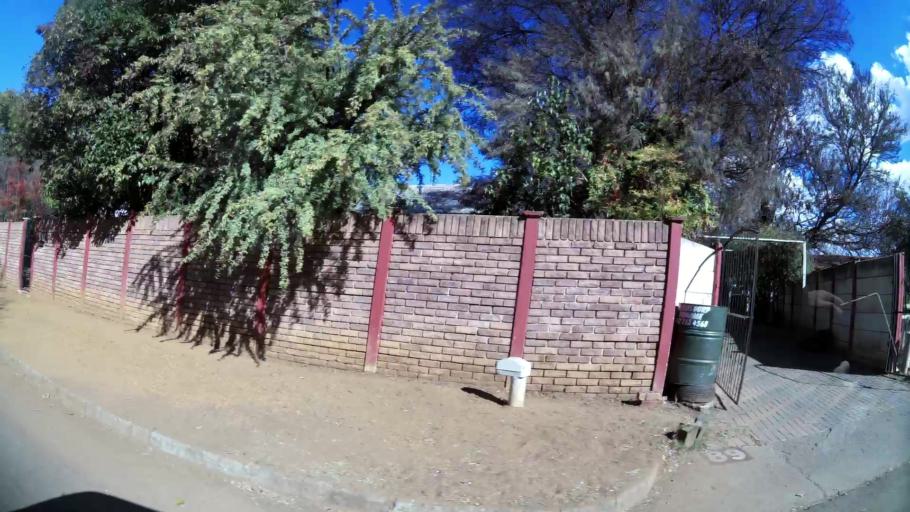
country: ZA
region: North-West
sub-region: Dr Kenneth Kaunda District Municipality
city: Klerksdorp
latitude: -26.8548
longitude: 26.6517
